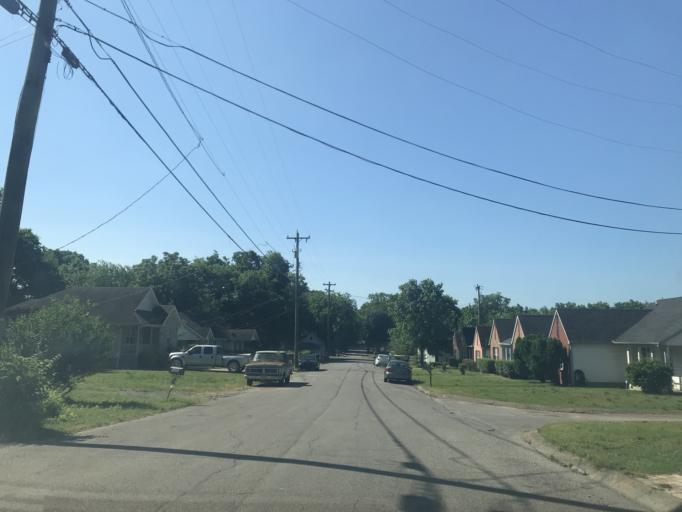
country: US
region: Tennessee
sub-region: Davidson County
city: Nashville
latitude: 36.1856
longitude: -86.8059
